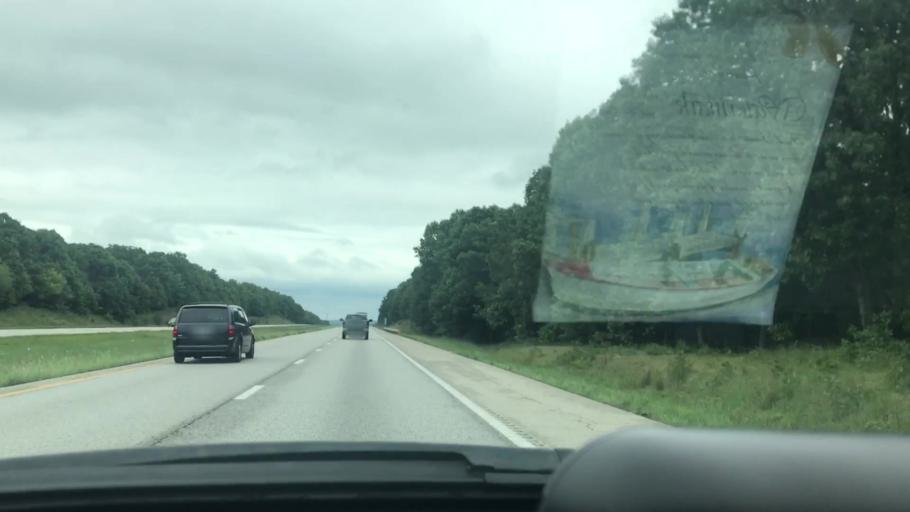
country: US
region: Missouri
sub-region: Lawrence County
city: Mount Vernon
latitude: 37.1431
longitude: -93.7158
